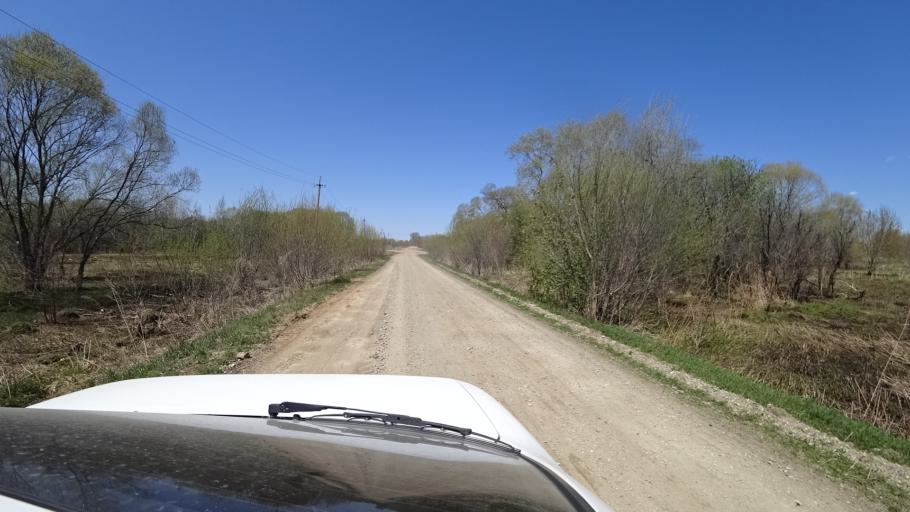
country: RU
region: Primorskiy
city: Lazo
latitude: 45.7949
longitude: 133.7630
